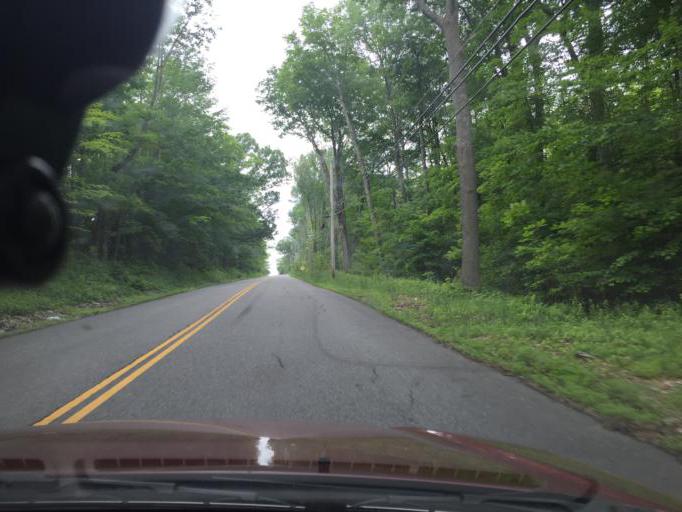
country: US
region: Connecticut
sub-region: Litchfield County
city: Litchfield
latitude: 41.7566
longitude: -73.2273
